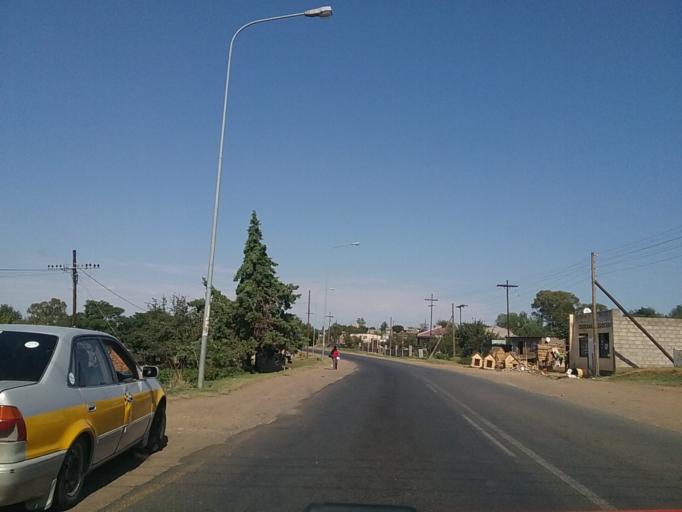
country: LS
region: Berea
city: Teyateyaneng
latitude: -29.1412
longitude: 27.7541
